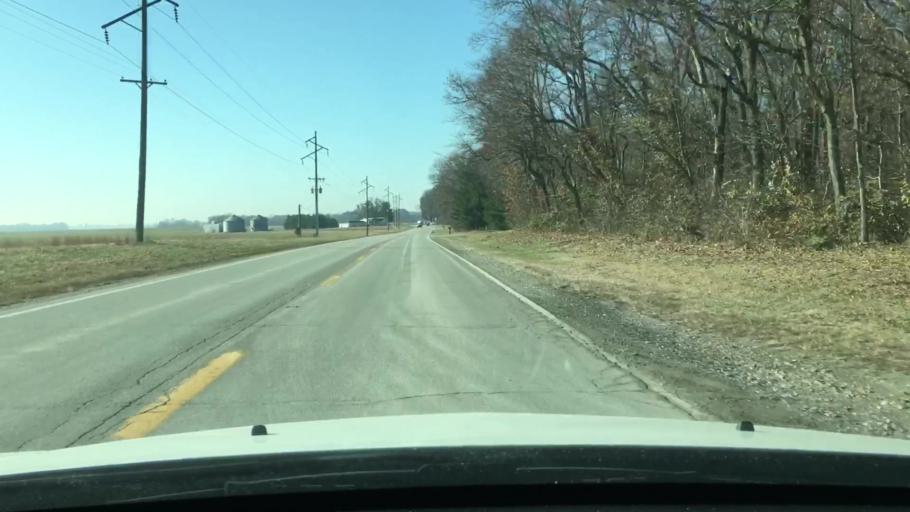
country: US
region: Illinois
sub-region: Cass County
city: Beardstown
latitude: 39.9811
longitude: -90.4510
